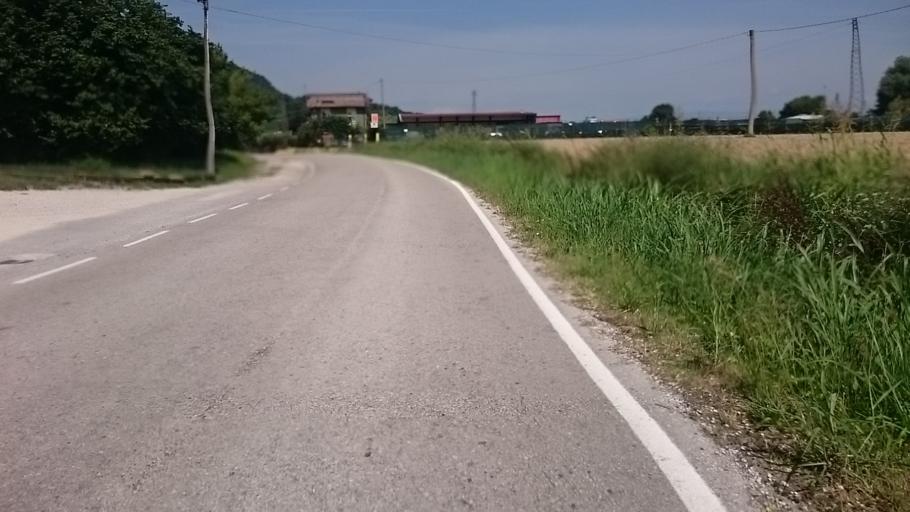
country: IT
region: Veneto
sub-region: Provincia di Vicenza
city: Longare
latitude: 45.4671
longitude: 11.6154
